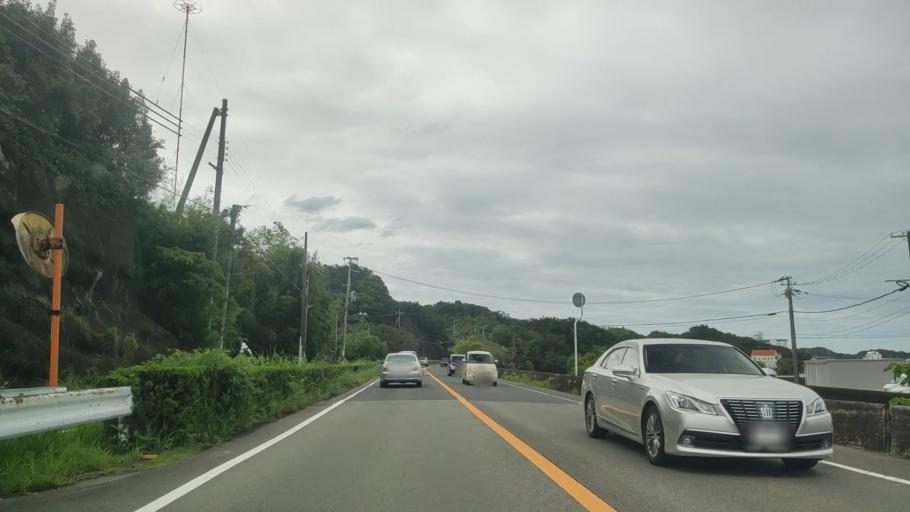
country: JP
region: Wakayama
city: Tanabe
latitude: 33.7041
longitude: 135.3966
